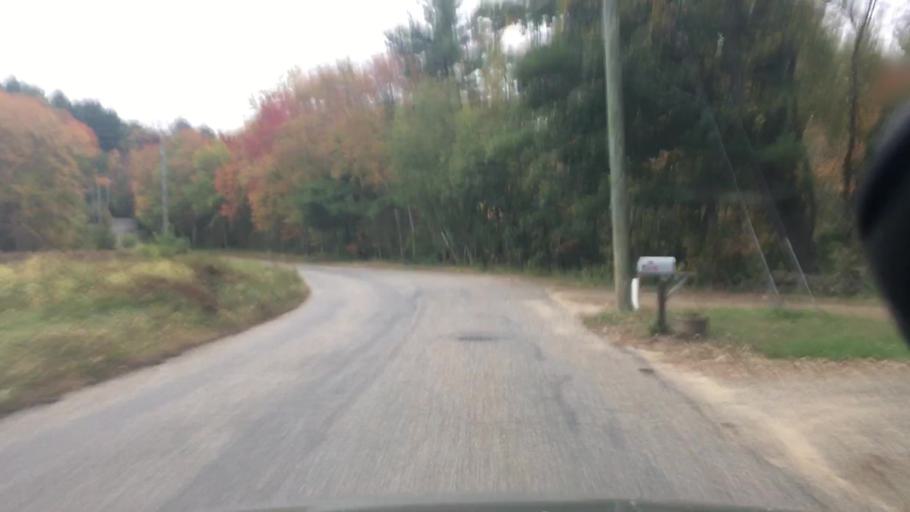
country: US
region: Connecticut
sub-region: Tolland County
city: Stafford
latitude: 41.9696
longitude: -72.2880
